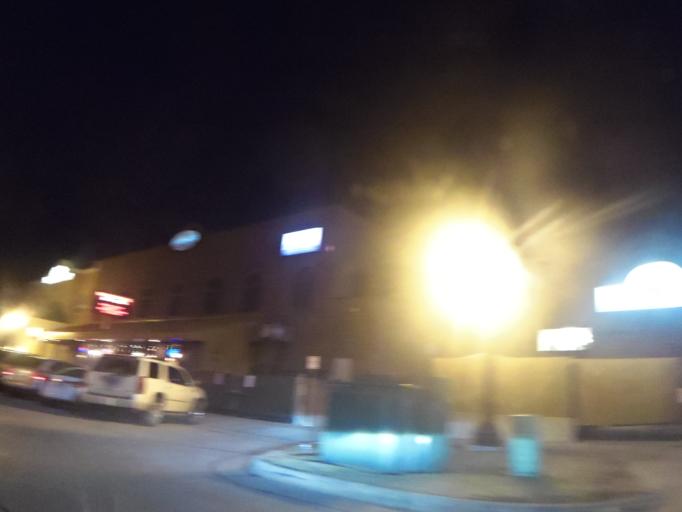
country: US
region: Minnesota
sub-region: Polk County
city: East Grand Forks
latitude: 47.9289
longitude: -97.0277
